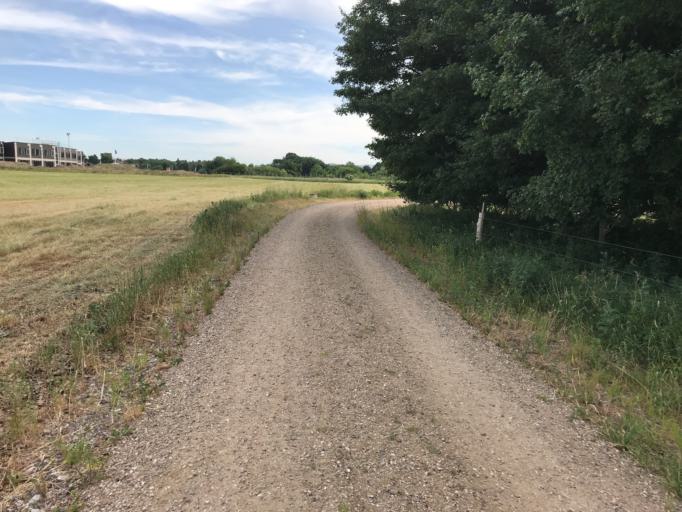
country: DK
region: Capital Region
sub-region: Ballerup Kommune
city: Malov
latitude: 55.7675
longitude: 12.3054
